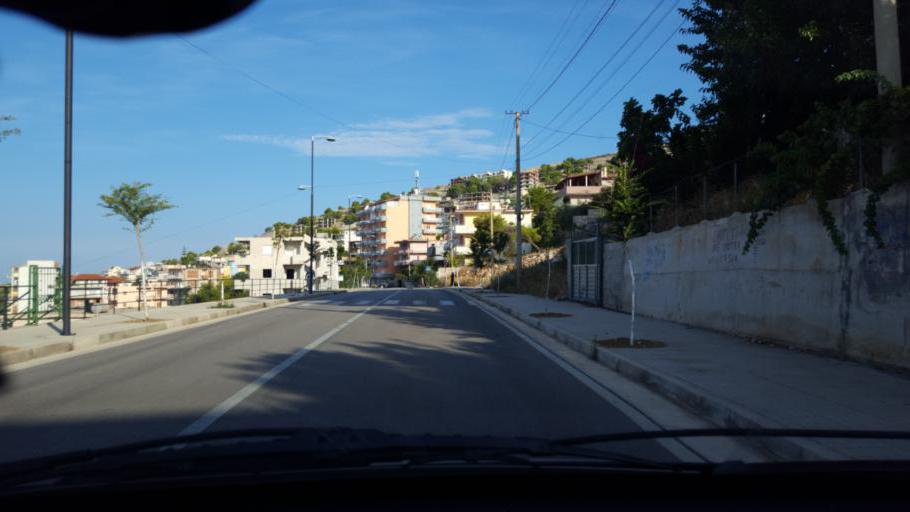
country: AL
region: Vlore
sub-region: Rrethi i Sarandes
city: Sarande
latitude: 39.8754
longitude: 19.9979
